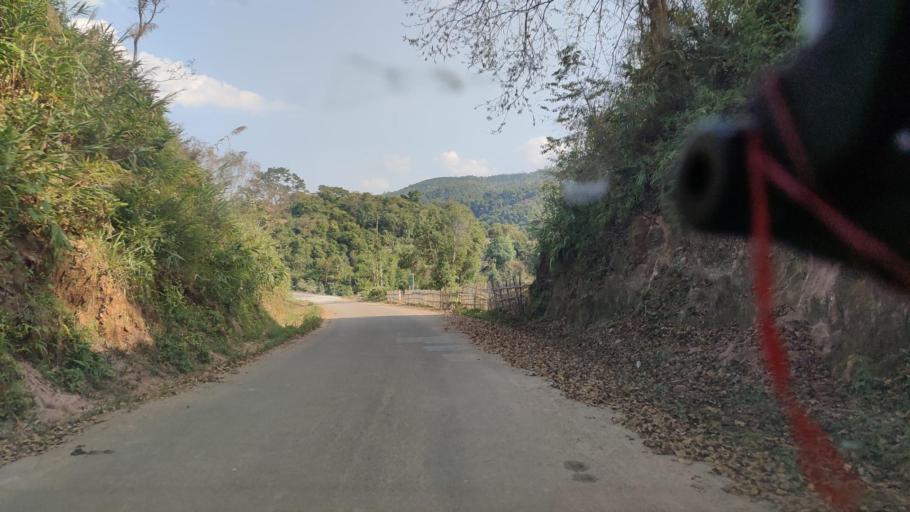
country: CN
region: Yunnan
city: Menghai
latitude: 21.4490
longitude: 99.6702
